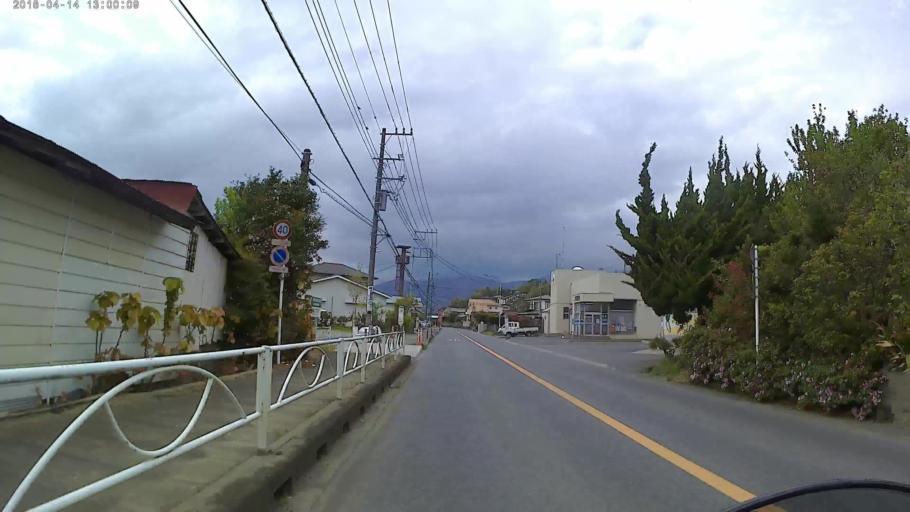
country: JP
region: Kanagawa
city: Isehara
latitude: 35.3712
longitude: 139.3077
